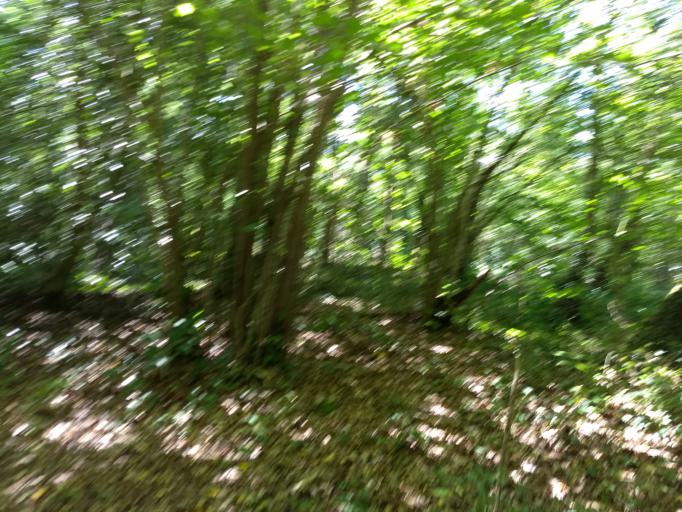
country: GB
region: England
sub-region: Isle of Wight
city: Newport
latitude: 50.7199
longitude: -1.2588
